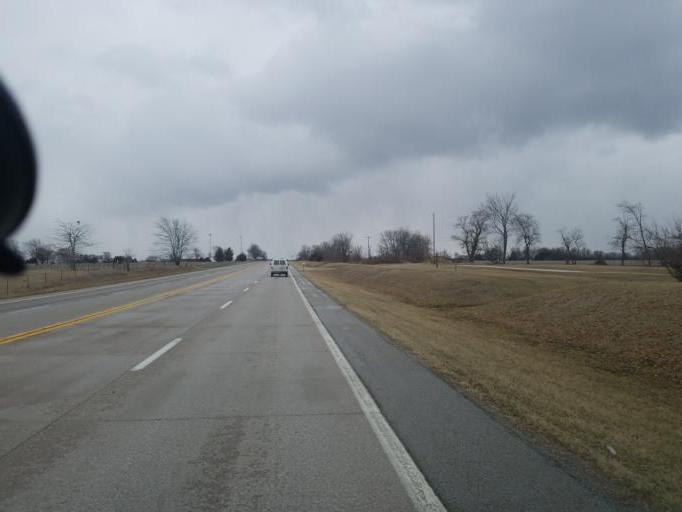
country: US
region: Missouri
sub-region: Macon County
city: Macon
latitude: 39.7741
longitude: -92.4752
